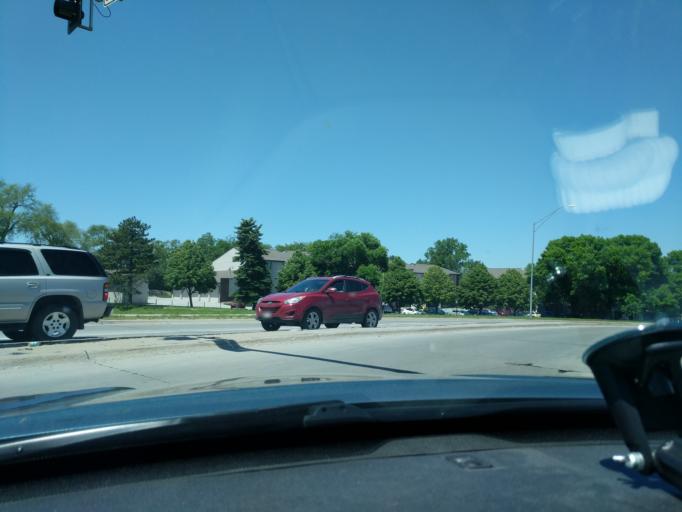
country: US
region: Nebraska
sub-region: Douglas County
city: Ralston
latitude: 41.2345
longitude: -96.0257
